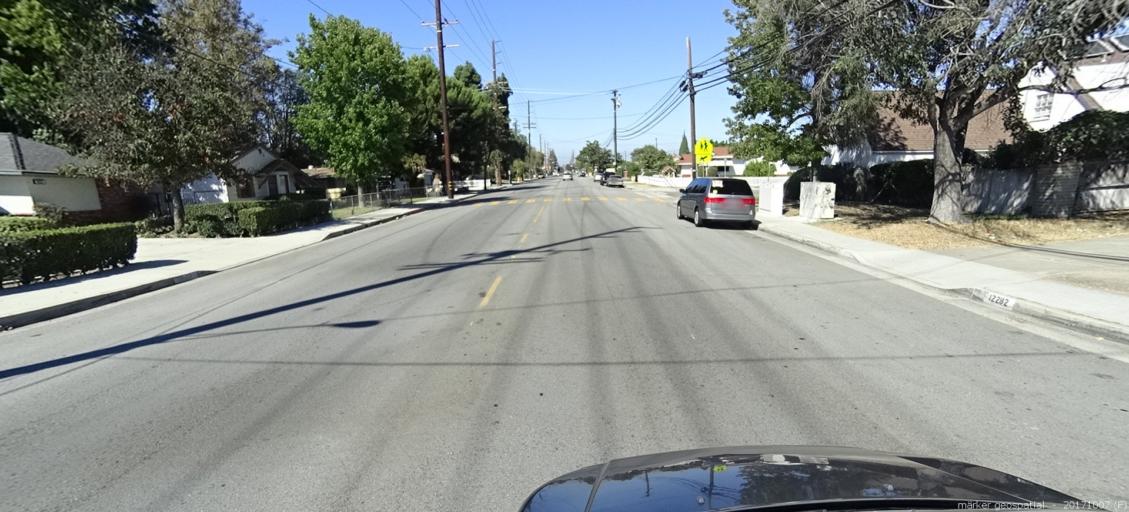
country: US
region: California
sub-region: Orange County
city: Stanton
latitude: 33.7841
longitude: -117.9840
